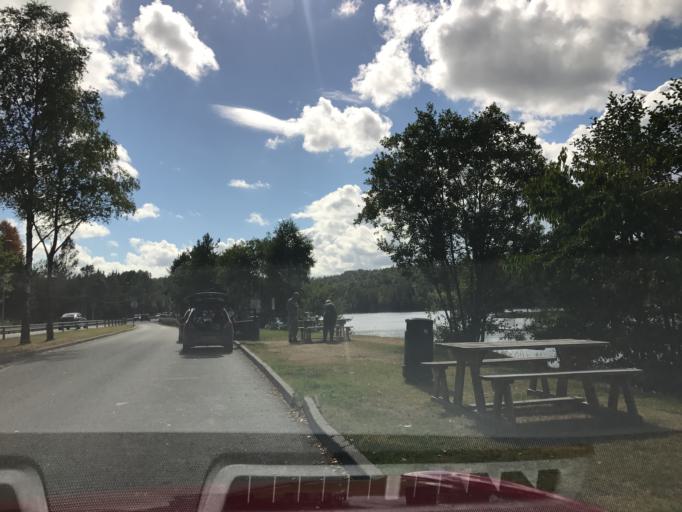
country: NO
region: Telemark
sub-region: Kragero
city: Kragero
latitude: 58.9584
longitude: 9.4353
